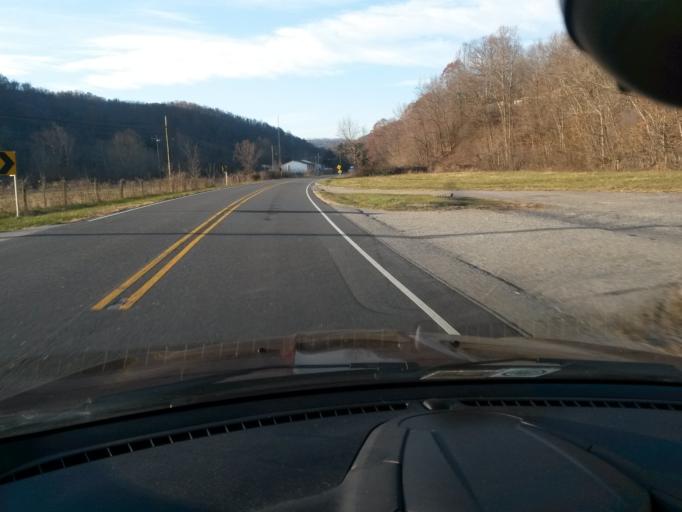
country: US
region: Virginia
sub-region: City of Buena Vista
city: Buena Vista
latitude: 37.6707
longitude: -79.2151
